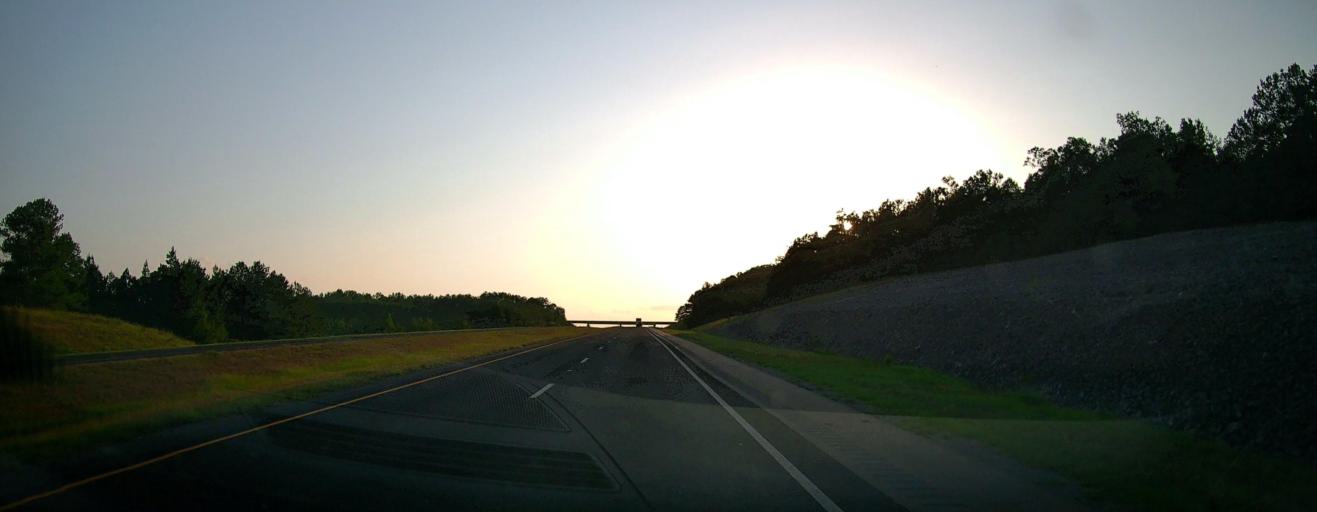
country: US
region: Alabama
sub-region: Marion County
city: Guin
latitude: 34.0461
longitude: -87.9098
